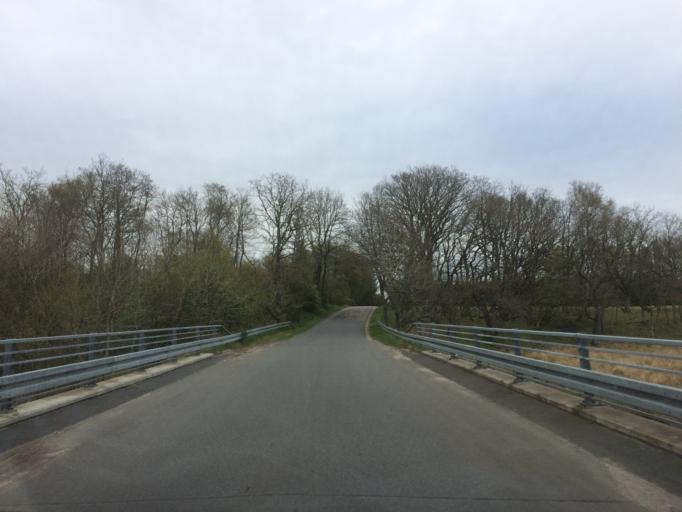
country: DK
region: Central Jutland
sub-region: Viborg Kommune
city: Karup
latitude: 56.3465
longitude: 9.1058
